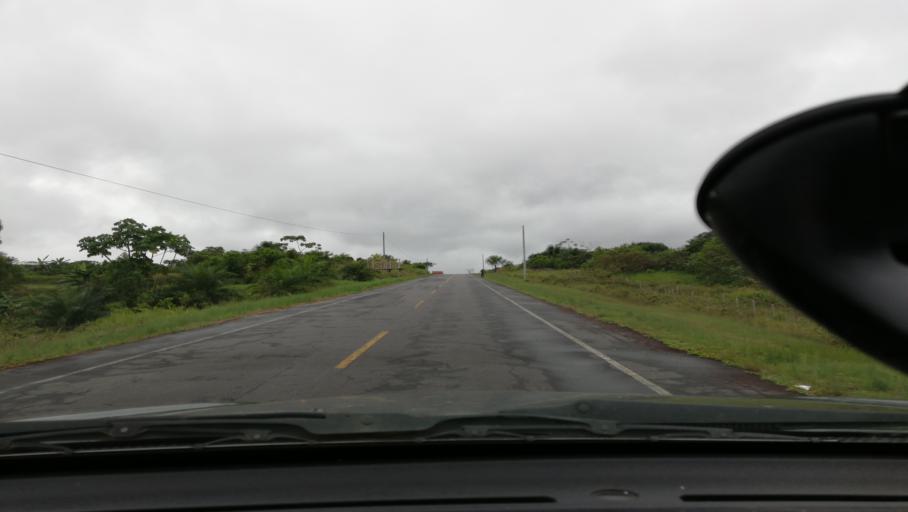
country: PE
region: Loreto
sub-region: Provincia de Loreto
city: Nauta
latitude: -4.3480
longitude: -73.5434
